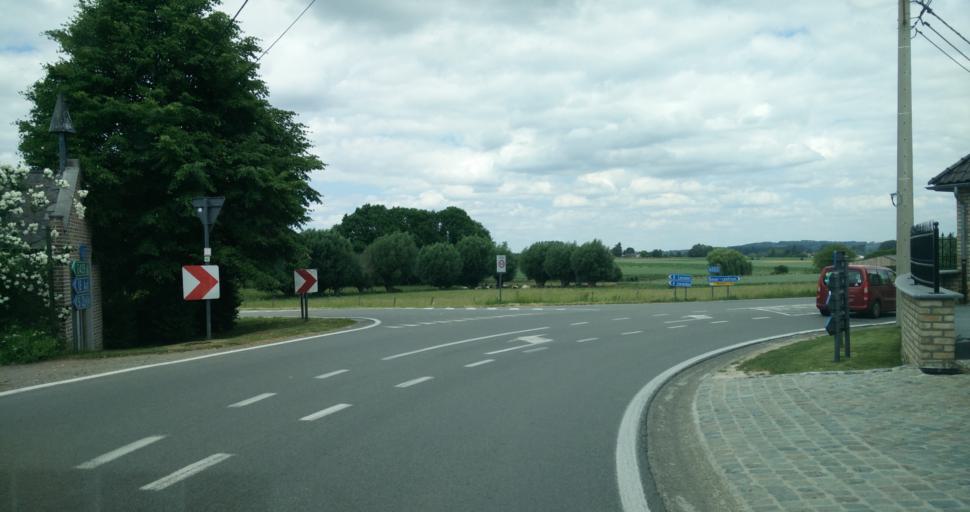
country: BE
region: Wallonia
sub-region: Province du Hainaut
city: Silly
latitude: 50.7085
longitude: 3.9297
